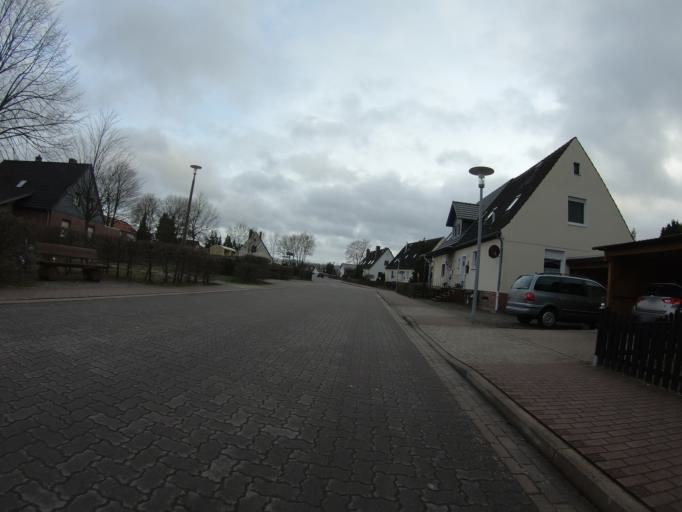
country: DE
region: Lower Saxony
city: Wesendorf
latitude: 52.5945
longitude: 10.5379
